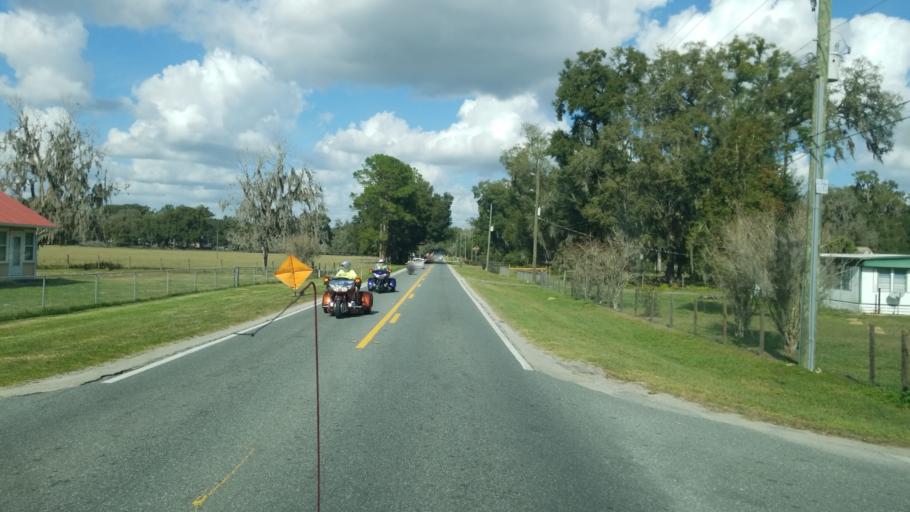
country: US
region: Florida
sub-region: Marion County
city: Belleview
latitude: 29.0037
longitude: -82.1199
